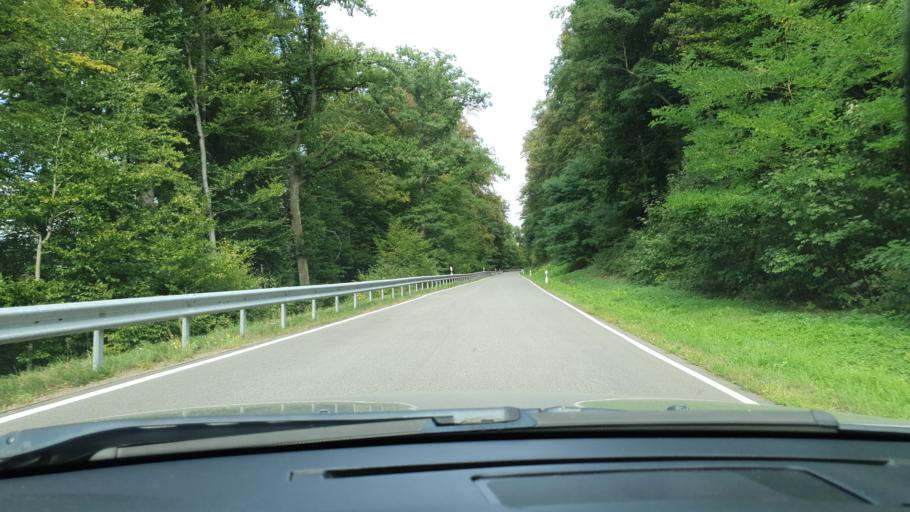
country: DE
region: Rheinland-Pfalz
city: Grossbundenbach
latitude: 49.3031
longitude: 7.4142
